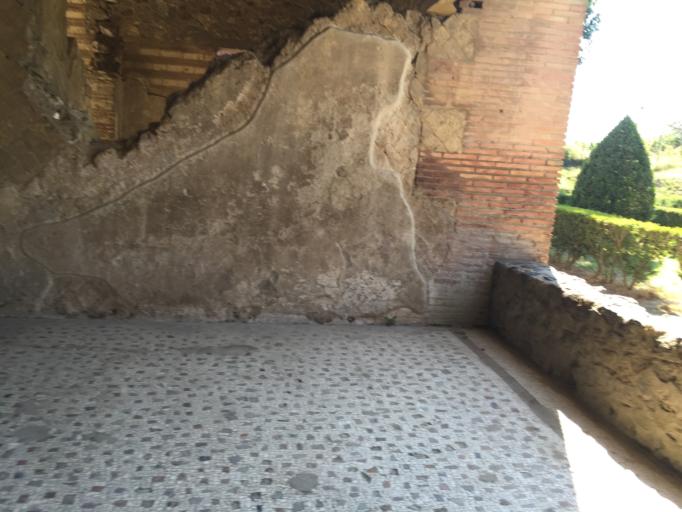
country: IT
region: Campania
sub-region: Provincia di Napoli
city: Torre Annunziata
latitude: 40.7539
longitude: 14.4773
